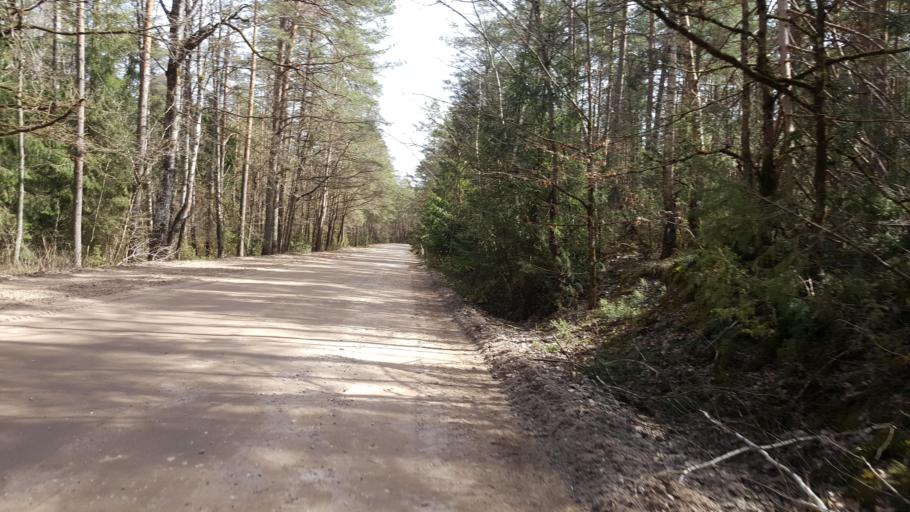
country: BY
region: Brest
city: Kamyanyuki
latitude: 52.5738
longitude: 23.7407
